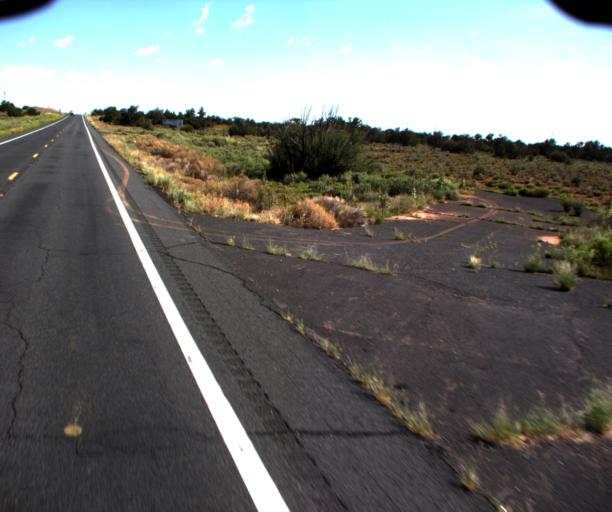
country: US
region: Arizona
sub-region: Coconino County
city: Williams
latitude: 35.6389
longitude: -112.1412
